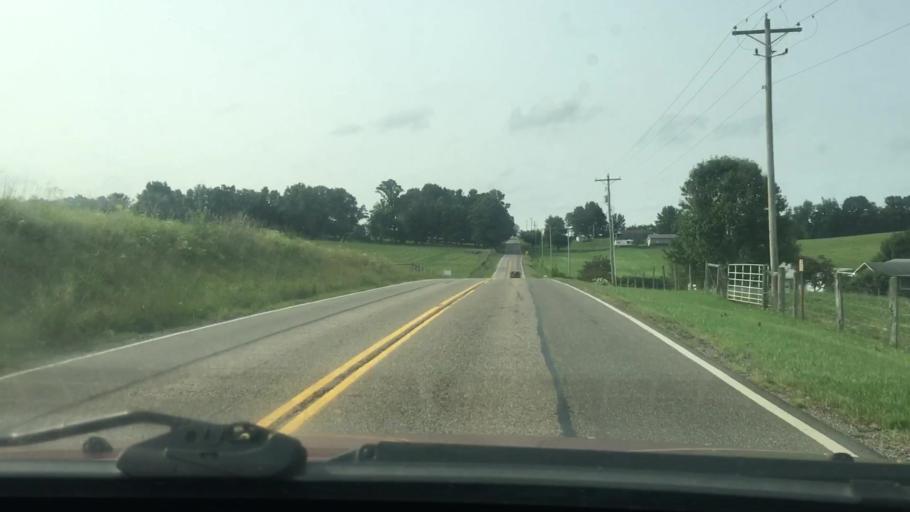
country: US
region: Ohio
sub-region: Belmont County
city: Barnesville
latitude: 40.1589
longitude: -81.2359
